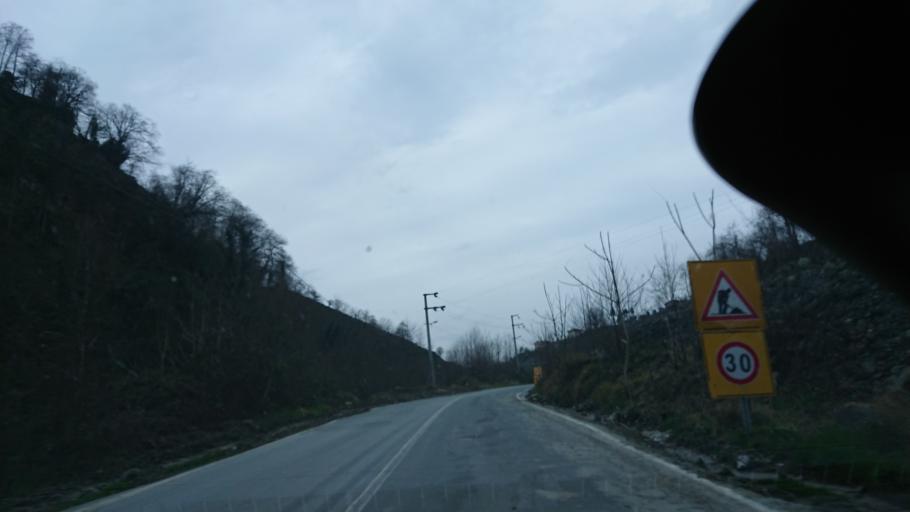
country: TR
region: Rize
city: Rize
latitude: 41.0207
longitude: 40.5023
